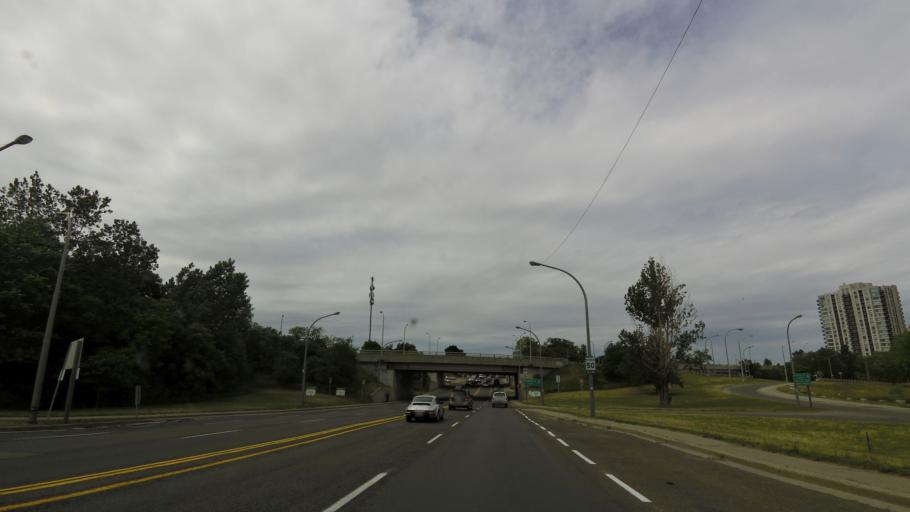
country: CA
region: Ontario
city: Etobicoke
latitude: 43.6401
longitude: -79.5346
